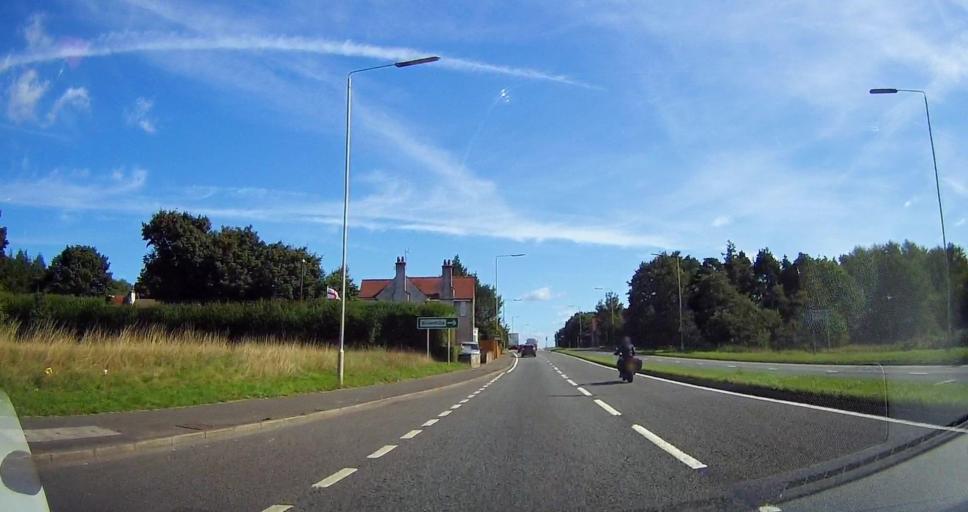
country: GB
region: England
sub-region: Staffordshire
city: Chasetown
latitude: 52.6564
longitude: -1.9419
